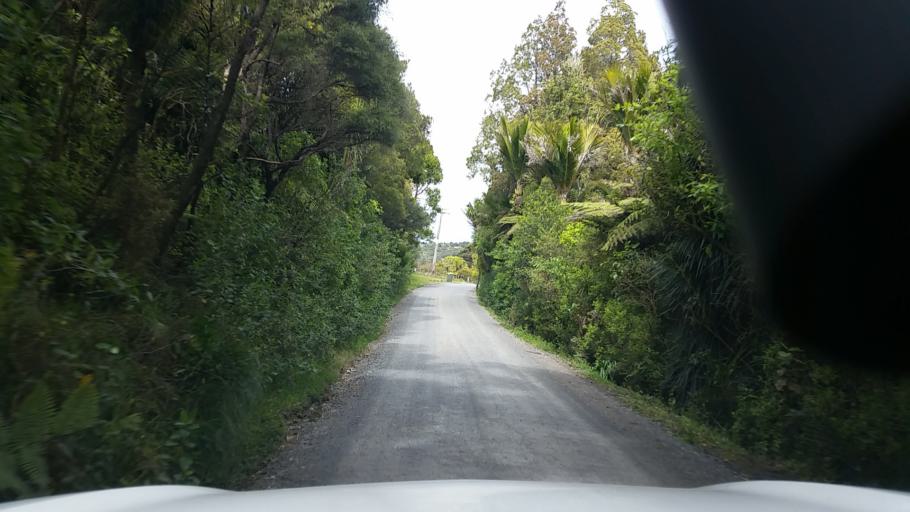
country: NZ
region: Auckland
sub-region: Auckland
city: Muriwai Beach
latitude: -36.8487
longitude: 174.5098
